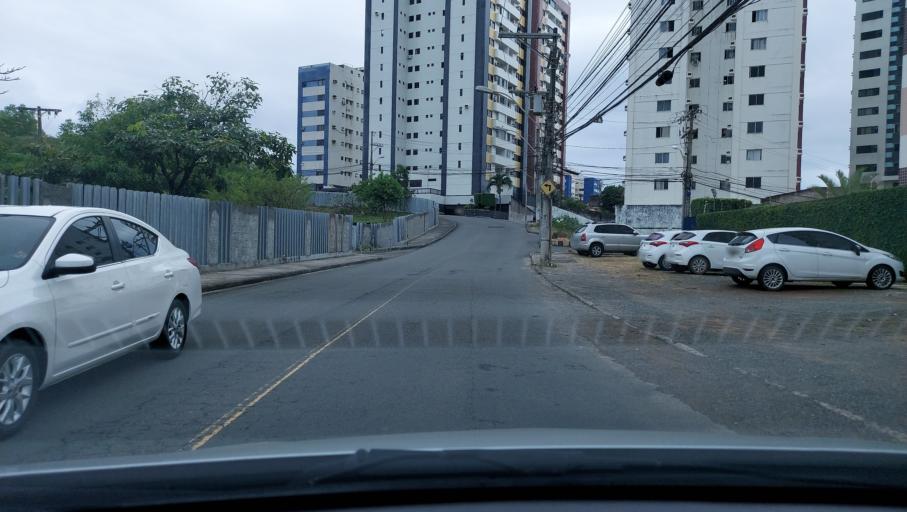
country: BR
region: Bahia
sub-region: Salvador
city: Salvador
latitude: -12.9835
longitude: -38.4423
